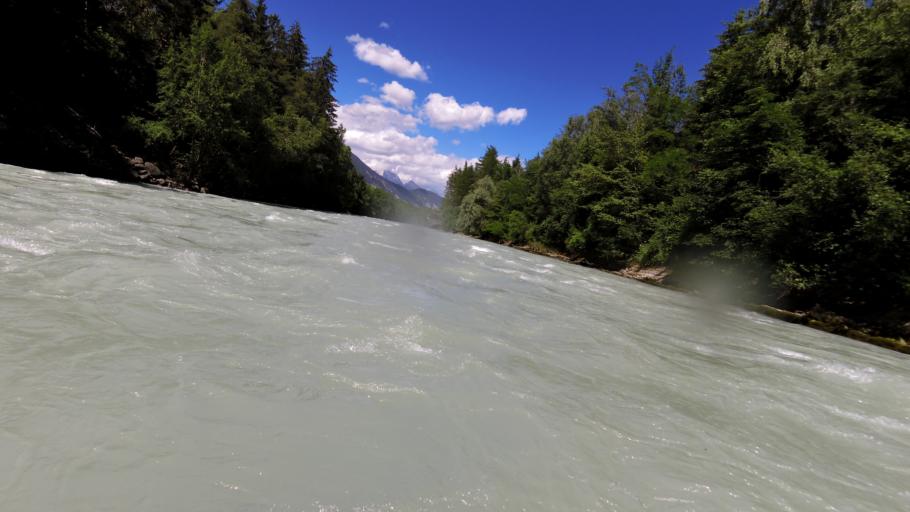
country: AT
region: Tyrol
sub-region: Politischer Bezirk Imst
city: Roppen
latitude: 47.2129
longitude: 10.8102
